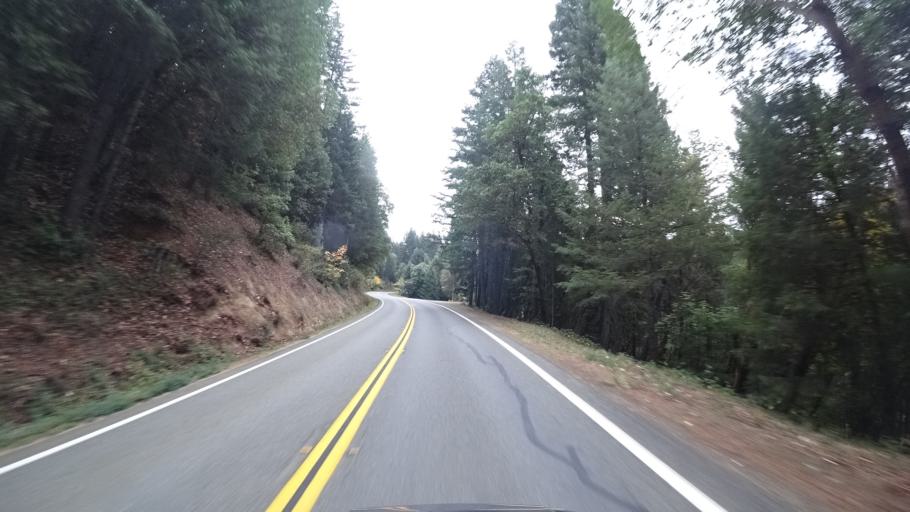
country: US
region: California
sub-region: Siskiyou County
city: Happy Camp
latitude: 41.7992
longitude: -123.3439
